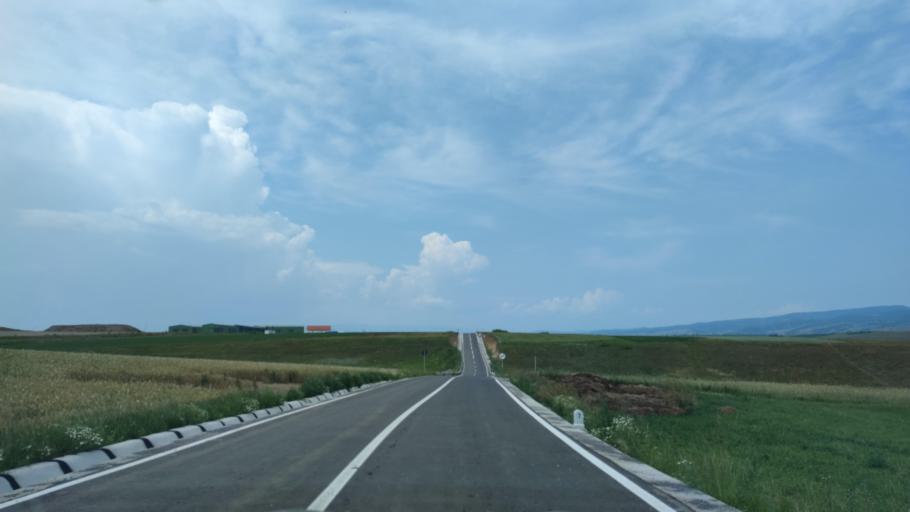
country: RO
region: Harghita
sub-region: Comuna Subcetate
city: Subcetate
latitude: 46.8229
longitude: 25.4472
